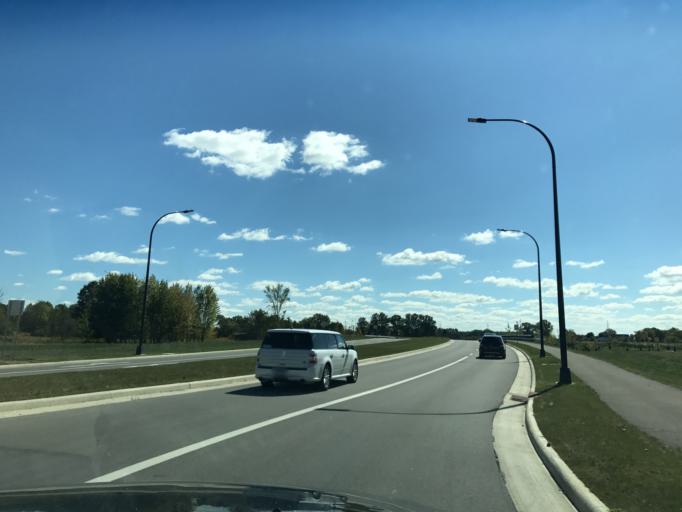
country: US
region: Ohio
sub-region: Delaware County
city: Delaware
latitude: 40.2352
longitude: -83.0955
